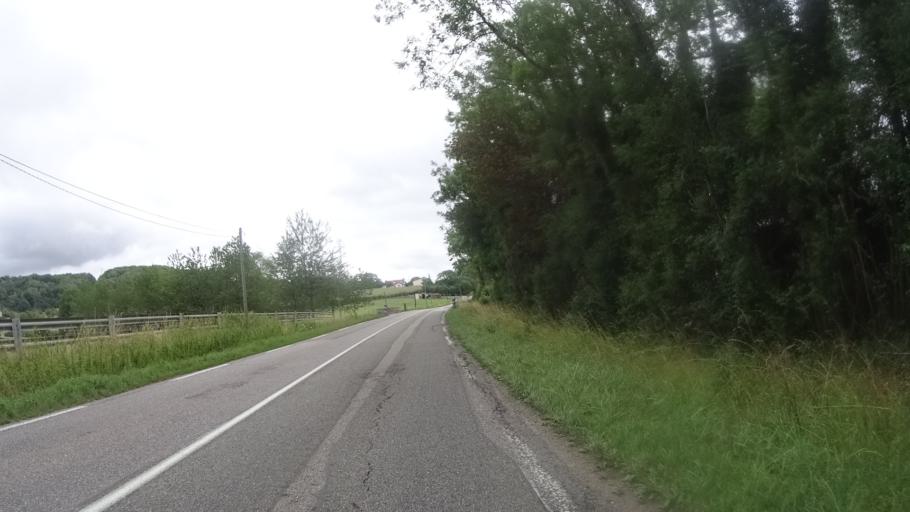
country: FR
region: Lorraine
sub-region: Departement de Meurthe-et-Moselle
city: Saint-Nicolas-de-Port
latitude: 48.6442
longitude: 6.2944
